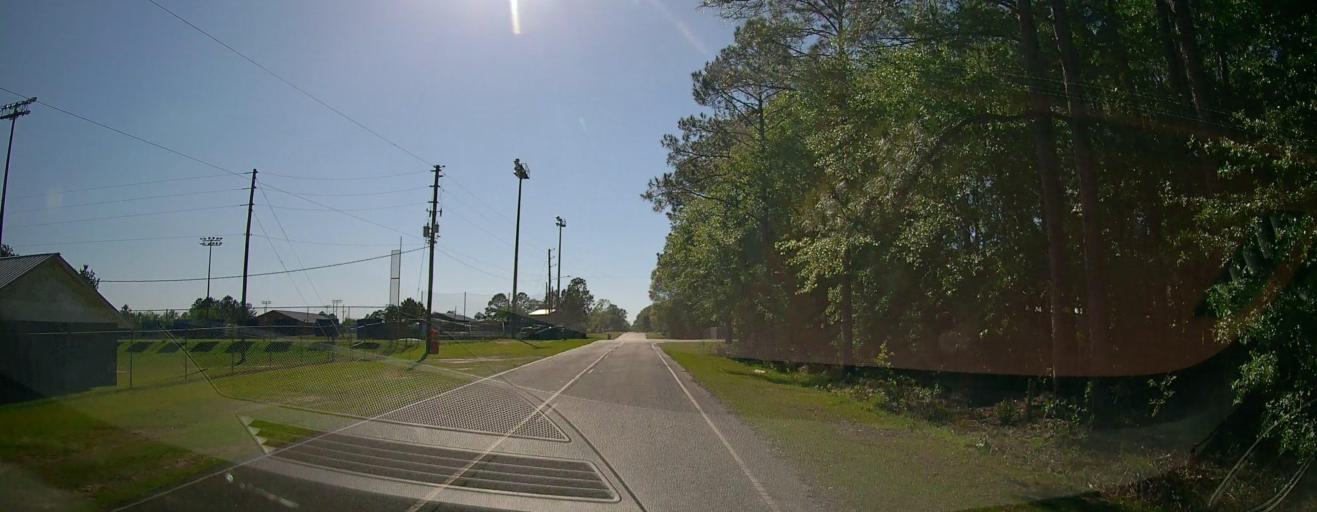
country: US
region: Georgia
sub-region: Wilcox County
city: Rochelle
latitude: 31.9440
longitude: -83.4486
